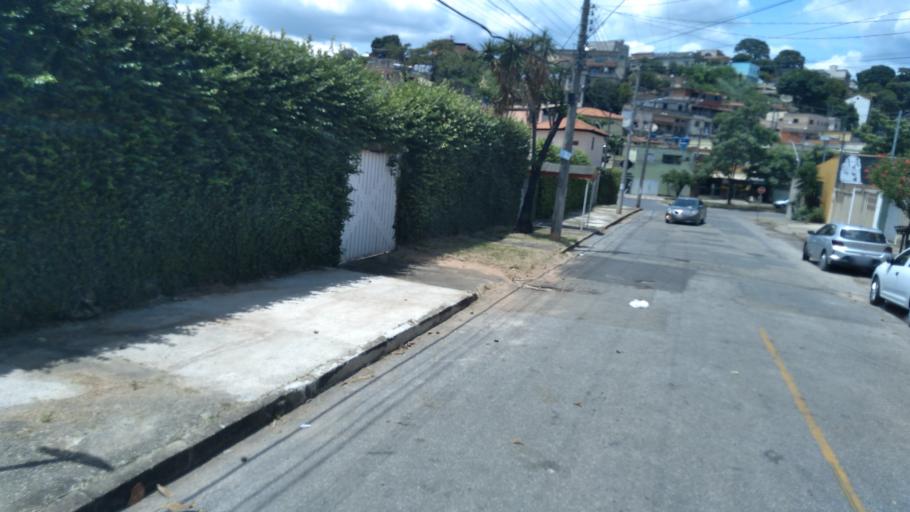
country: BR
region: Minas Gerais
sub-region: Contagem
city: Contagem
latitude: -19.9149
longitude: -44.0046
